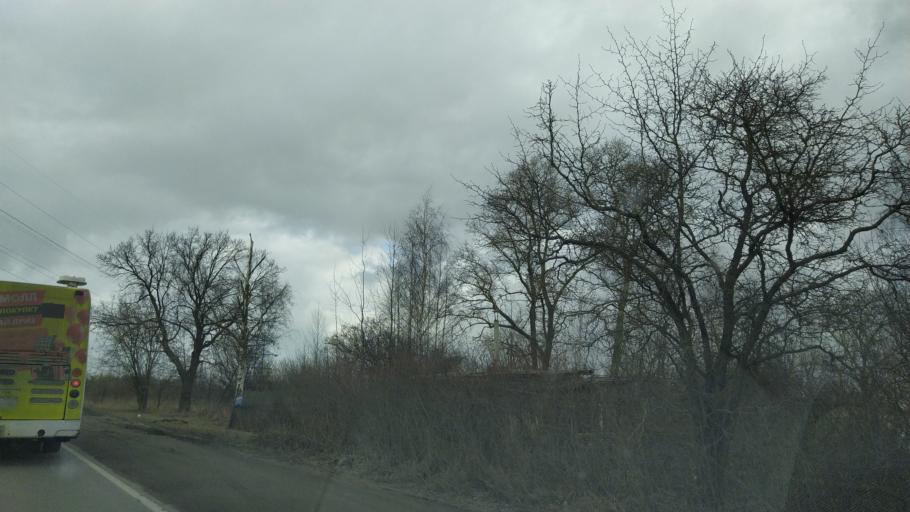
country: RU
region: St.-Petersburg
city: Tyarlevo
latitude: 59.7136
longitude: 30.4369
